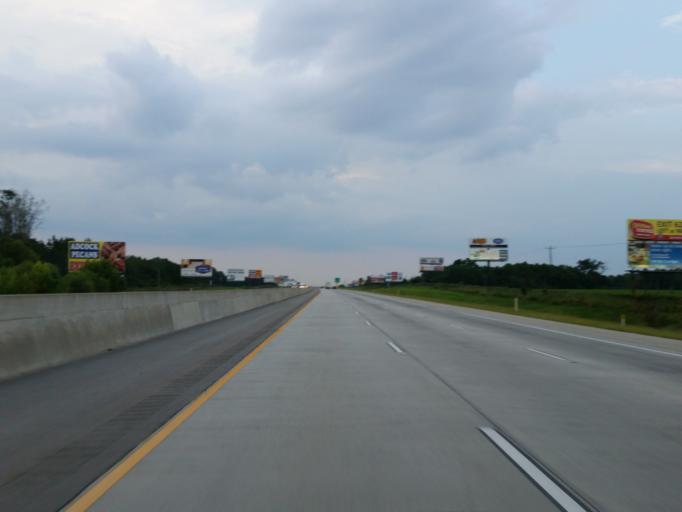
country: US
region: Georgia
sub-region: Tift County
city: Unionville
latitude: 31.3875
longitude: -83.4973
